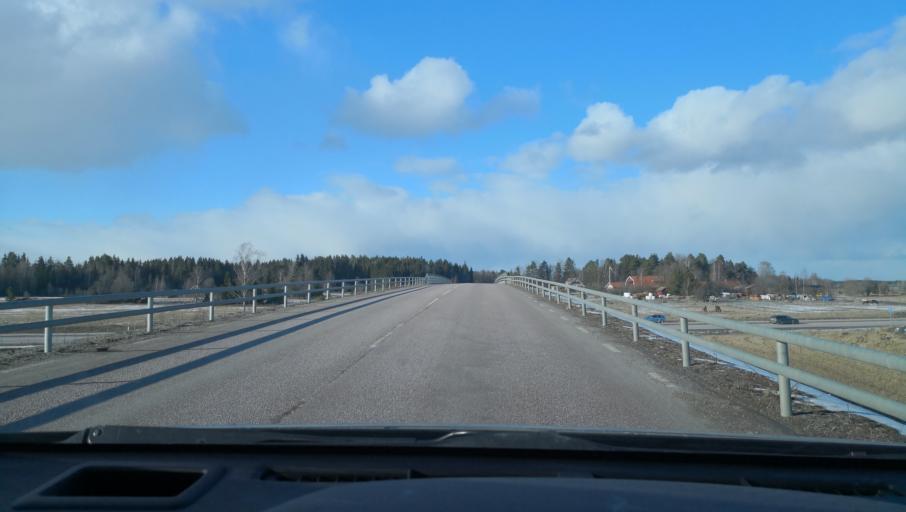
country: SE
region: Uppsala
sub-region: Enkopings Kommun
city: Hummelsta
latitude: 59.6432
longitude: 16.9661
